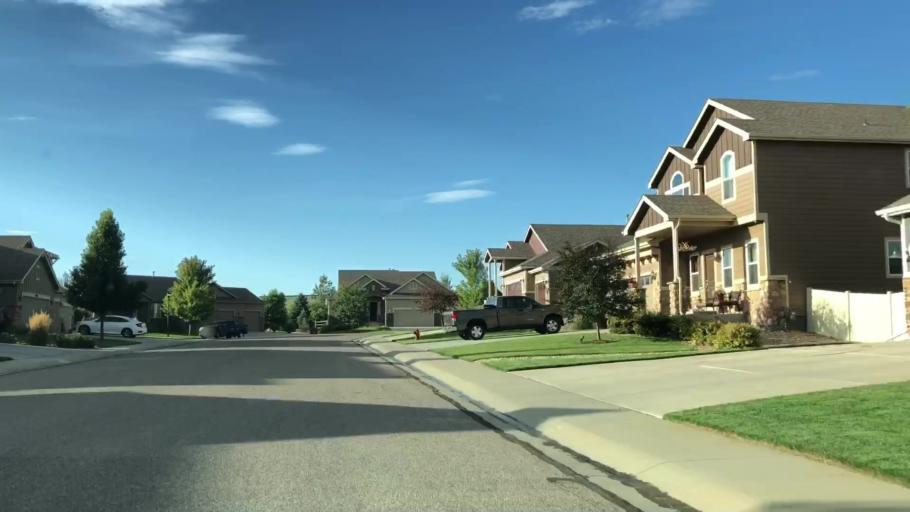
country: US
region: Colorado
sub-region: Weld County
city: Windsor
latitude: 40.4413
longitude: -104.9642
